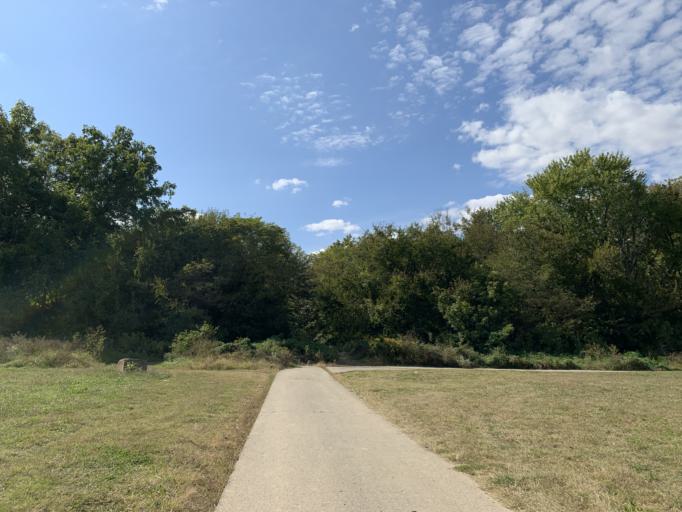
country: US
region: Indiana
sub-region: Floyd County
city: New Albany
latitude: 38.2785
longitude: -85.8028
